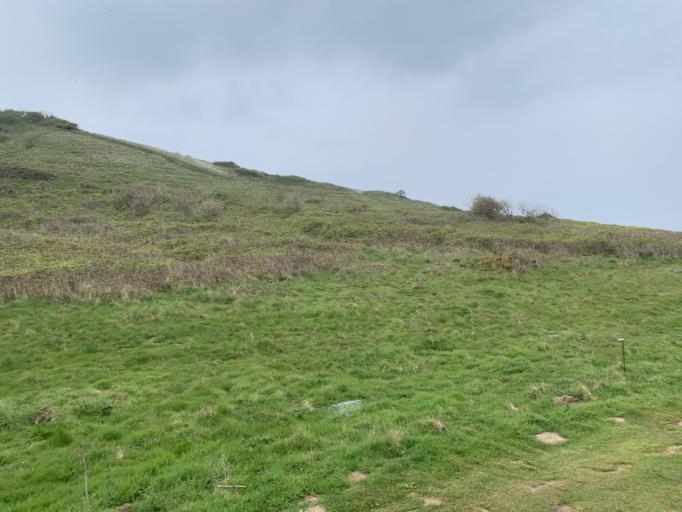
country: FR
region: Haute-Normandie
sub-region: Departement de la Seine-Maritime
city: Etretat
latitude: 49.6879
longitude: 0.1684
